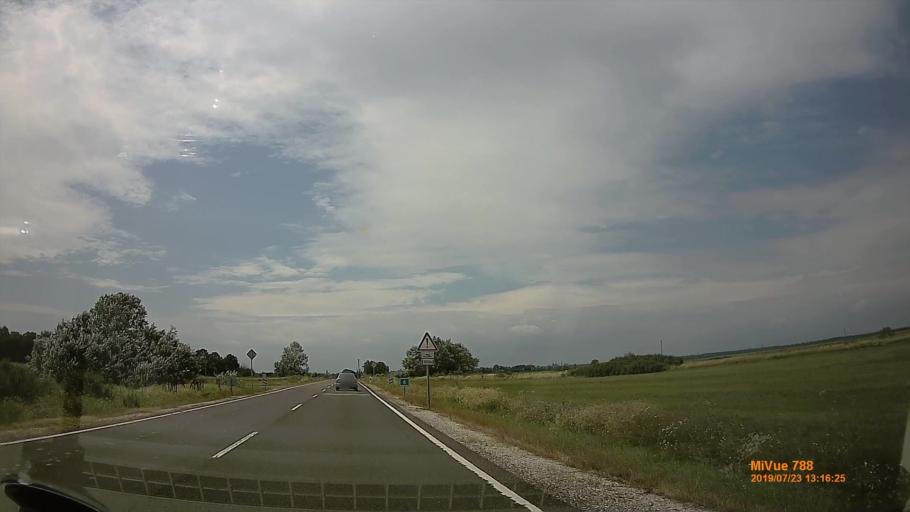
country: HU
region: Hajdu-Bihar
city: Polgar
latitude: 47.9086
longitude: 21.1707
